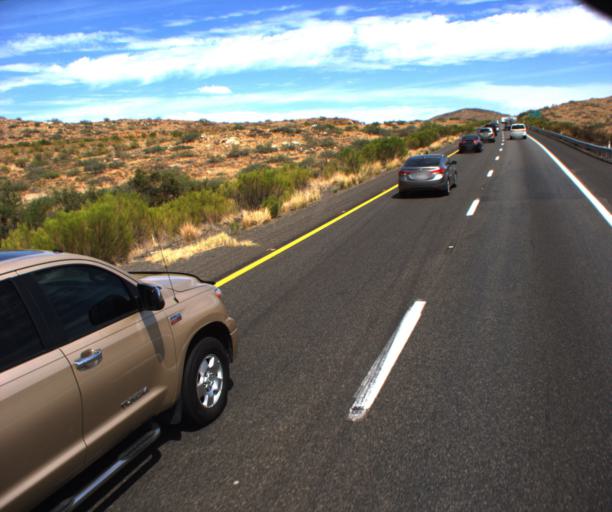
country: US
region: Arizona
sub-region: Yavapai County
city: Cordes Lakes
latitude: 34.2770
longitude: -112.1152
